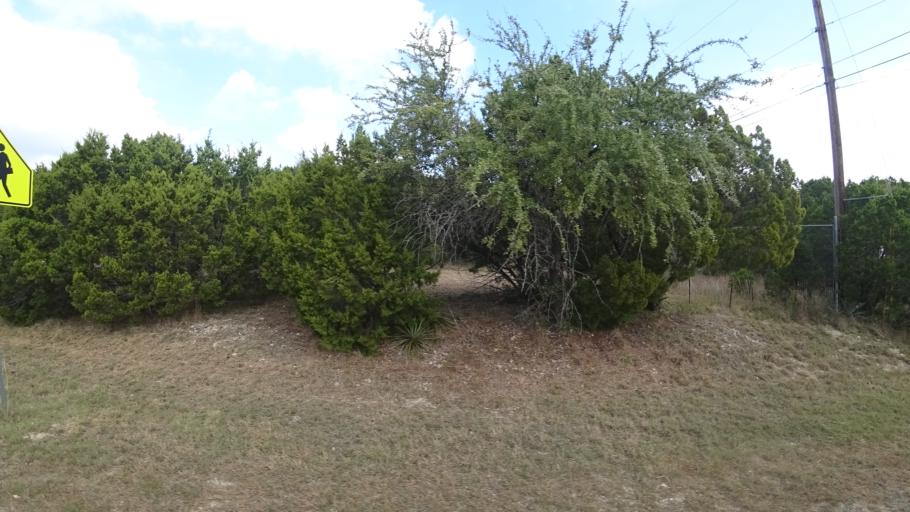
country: US
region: Texas
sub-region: Travis County
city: Barton Creek
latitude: 30.3069
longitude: -97.8798
